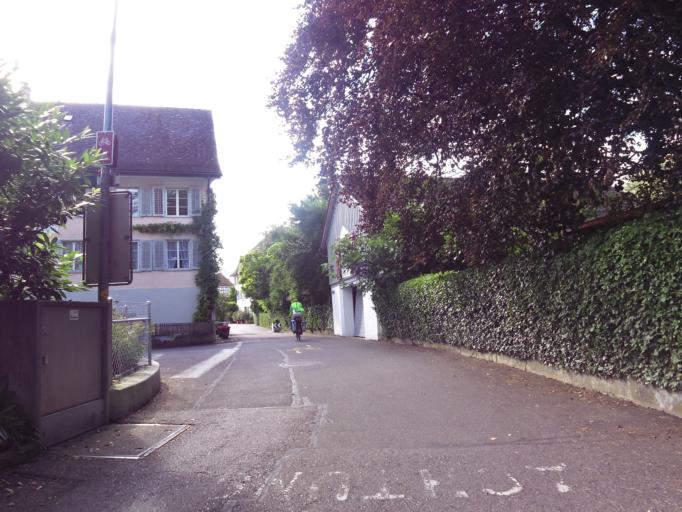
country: CH
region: Thurgau
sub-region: Arbon District
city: Uttwil
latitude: 47.5852
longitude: 9.3458
